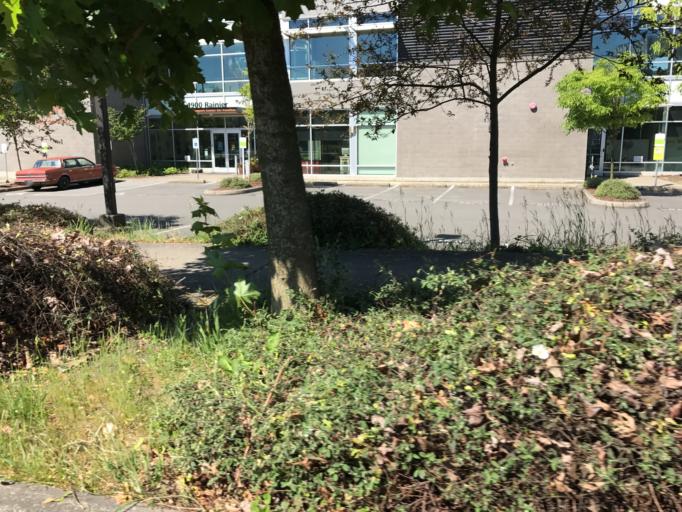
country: US
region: Washington
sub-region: King County
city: Seattle
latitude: 47.5860
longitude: -122.3030
